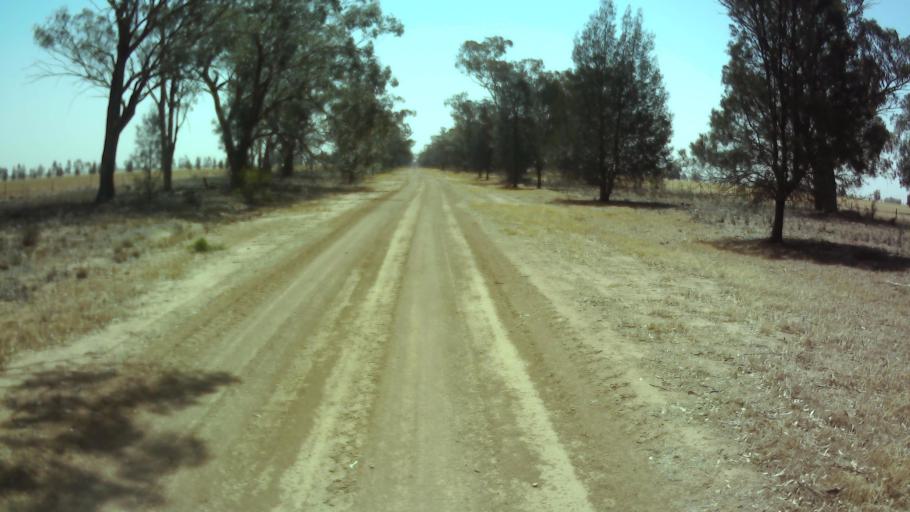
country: AU
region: New South Wales
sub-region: Weddin
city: Grenfell
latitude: -33.9329
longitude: 147.8015
